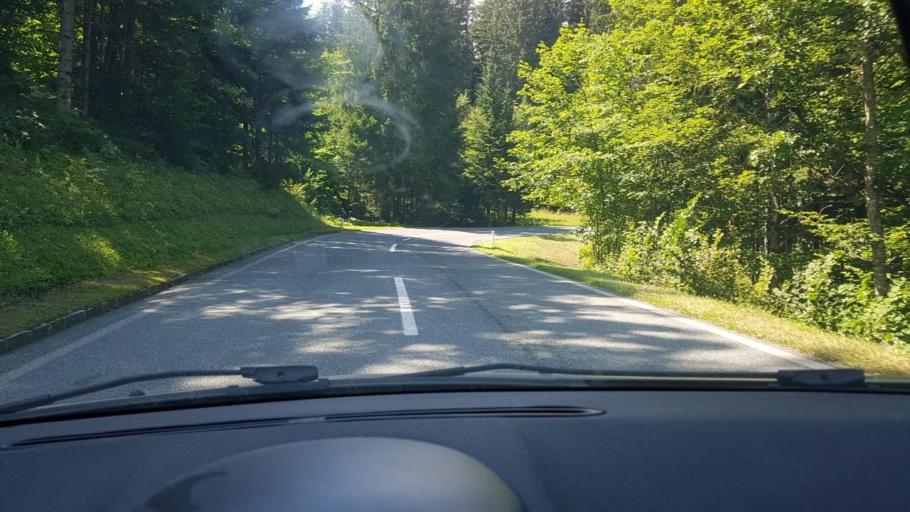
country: SI
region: Jezersko
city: Zgornje Jezersko
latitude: 46.4225
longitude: 14.5447
